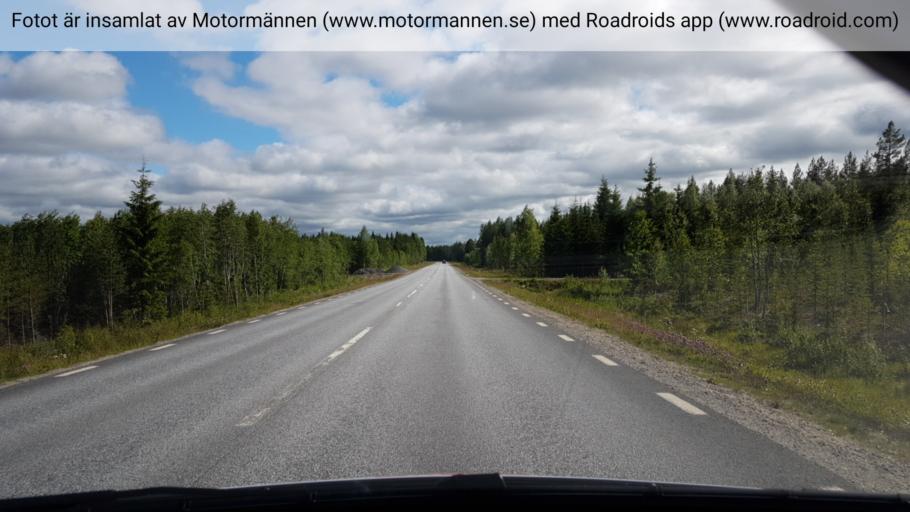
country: SE
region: Vaesterbotten
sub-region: Vannas Kommun
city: Vaennaes
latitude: 63.9545
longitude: 19.7559
